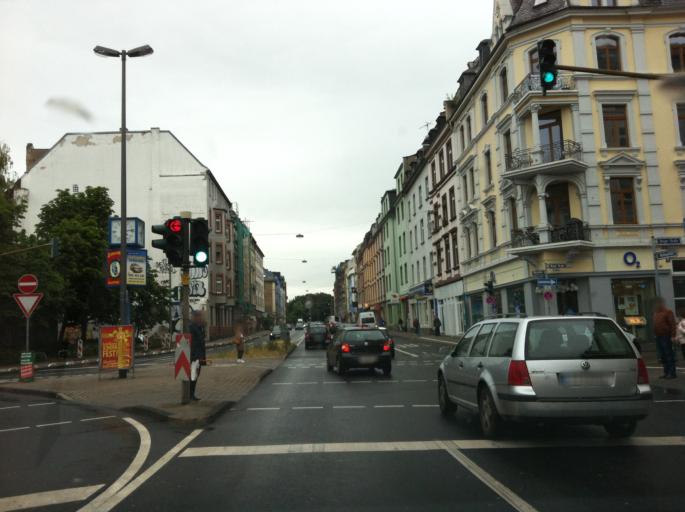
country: DE
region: Hesse
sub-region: Regierungsbezirk Darmstadt
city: Frankfurt am Main
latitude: 50.1230
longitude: 8.7017
